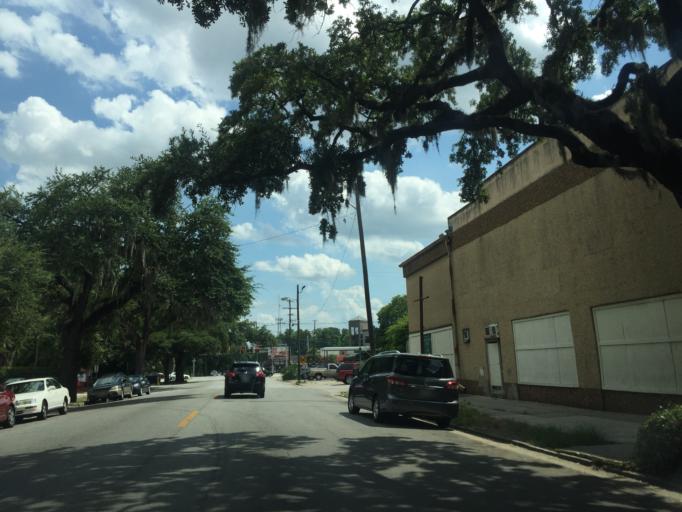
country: US
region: Georgia
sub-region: Chatham County
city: Savannah
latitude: 32.0536
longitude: -81.1017
